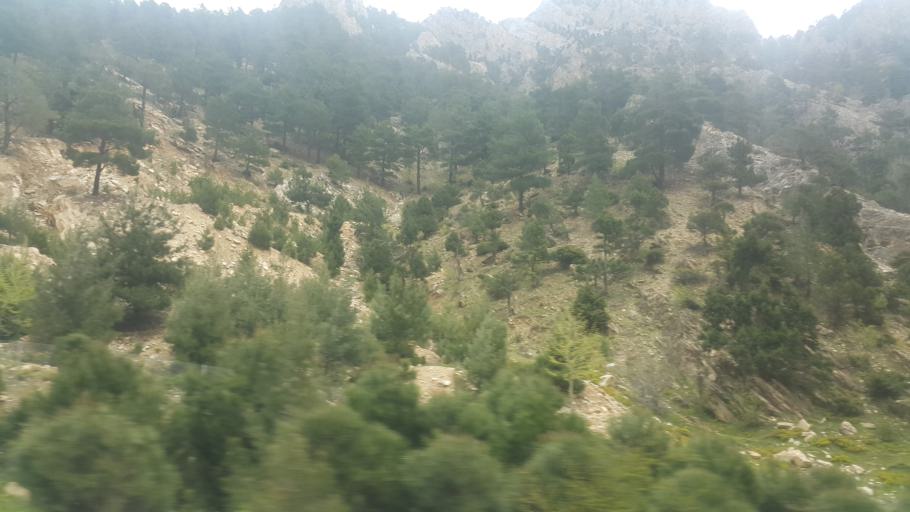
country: TR
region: Adana
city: Pozanti
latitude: 37.4854
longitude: 34.8484
